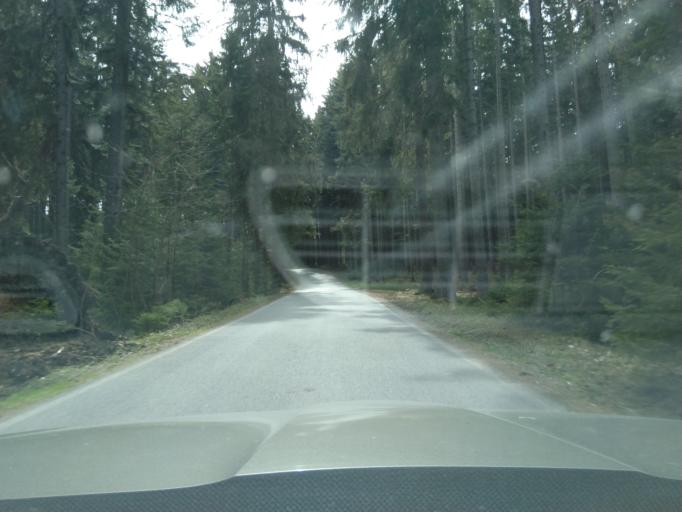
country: CZ
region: Jihocesky
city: Vacov
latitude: 49.1599
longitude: 13.6894
